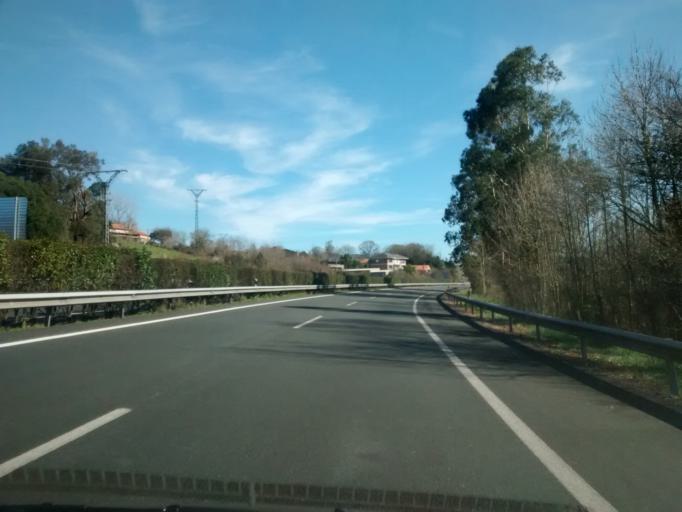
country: ES
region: Cantabria
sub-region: Provincia de Cantabria
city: Entrambasaguas
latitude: 43.3919
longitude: -3.6994
